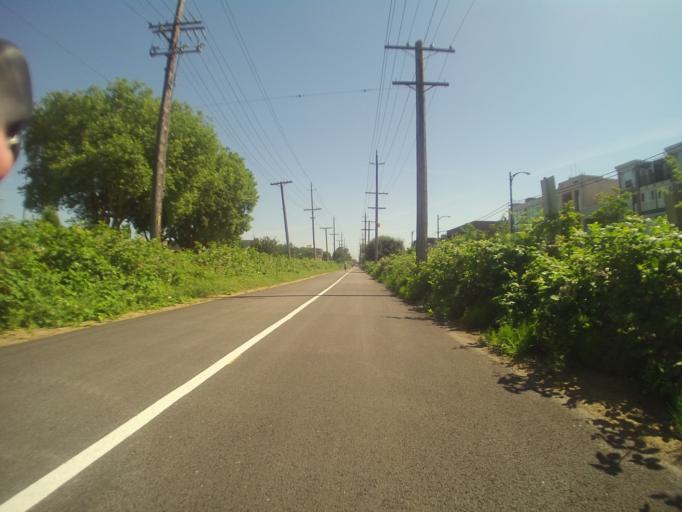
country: CA
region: British Columbia
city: Vancouver
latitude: 49.2376
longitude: -123.1553
